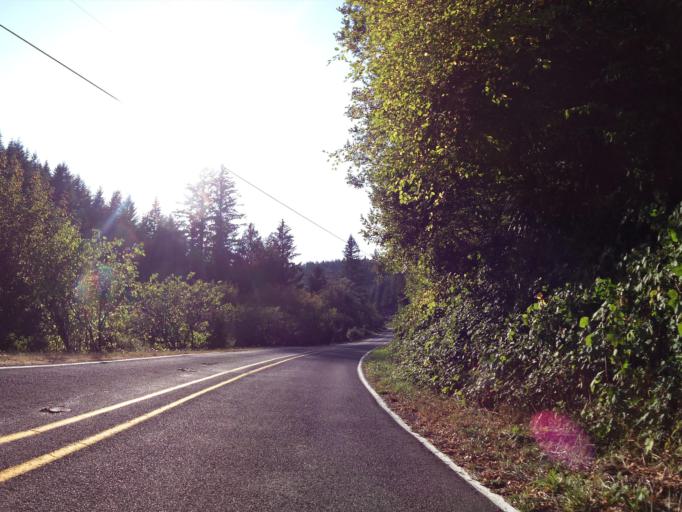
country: US
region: Oregon
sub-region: Lincoln County
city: Rose Lodge
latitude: 45.0324
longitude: -123.9264
